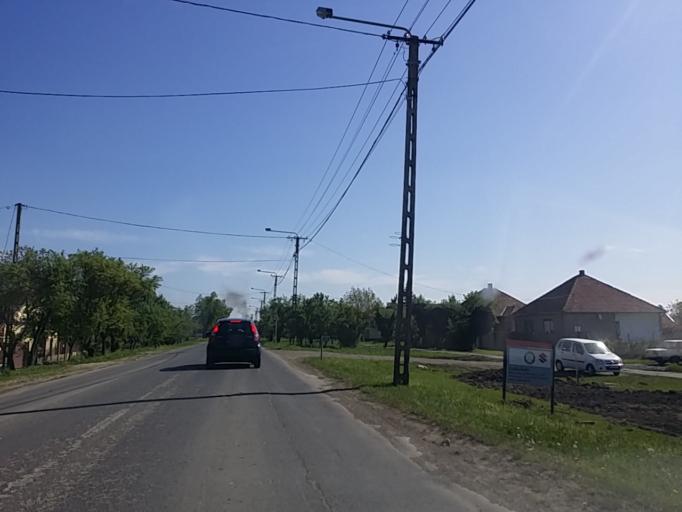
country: HU
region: Bekes
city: Doboz
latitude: 46.7315
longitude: 21.2346
